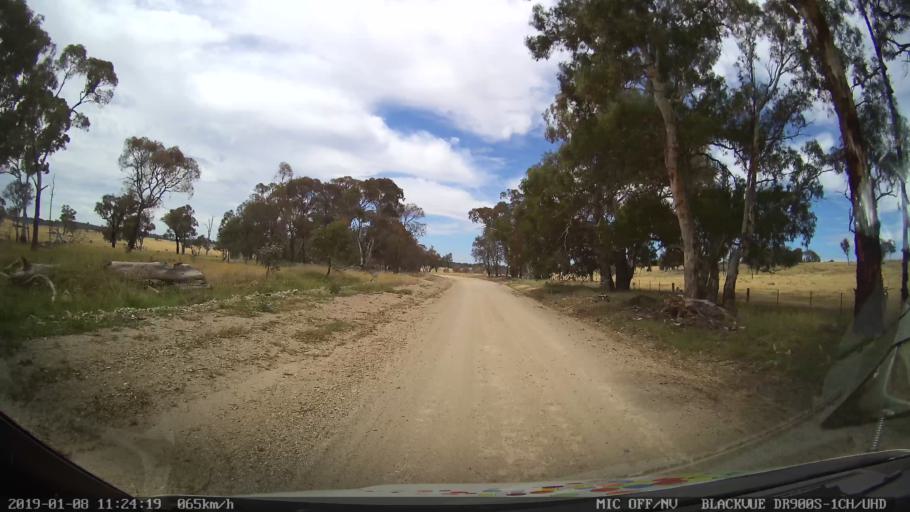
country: AU
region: New South Wales
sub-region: Guyra
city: Guyra
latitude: -30.2636
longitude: 151.5581
